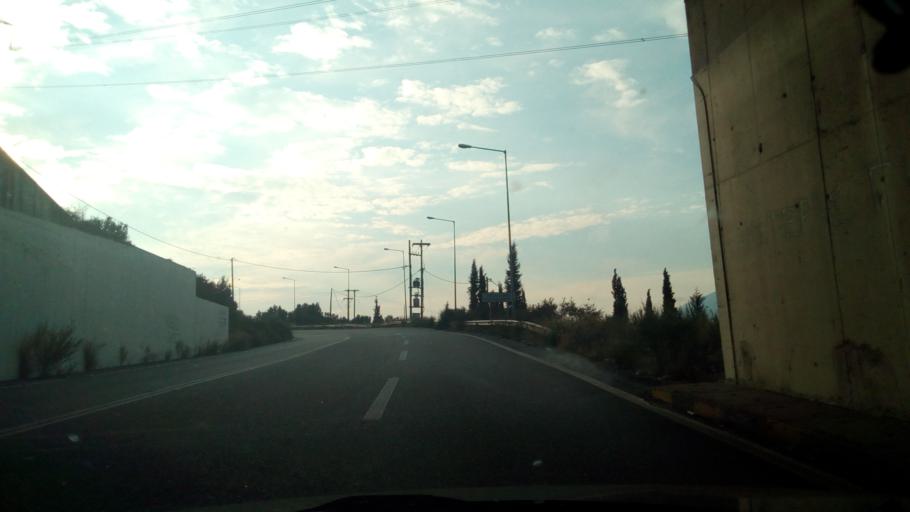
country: GR
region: West Greece
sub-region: Nomos Aitolias kai Akarnanias
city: Nafpaktos
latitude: 38.4023
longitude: 21.8103
